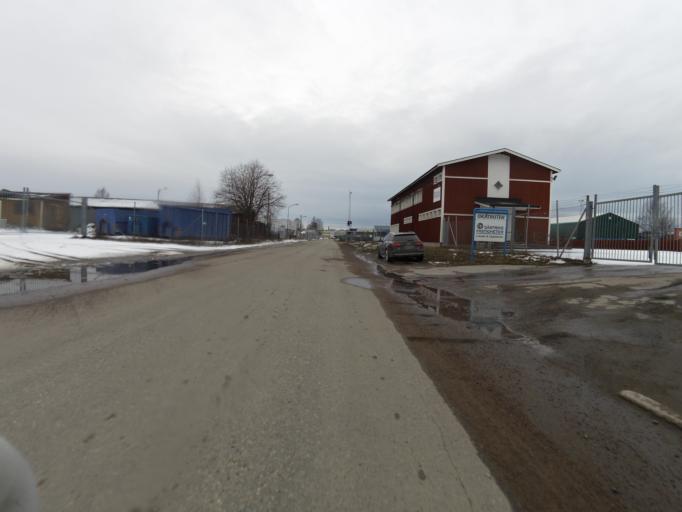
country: SE
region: Gaevleborg
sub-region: Gavle Kommun
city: Gavle
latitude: 60.6836
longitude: 17.1586
